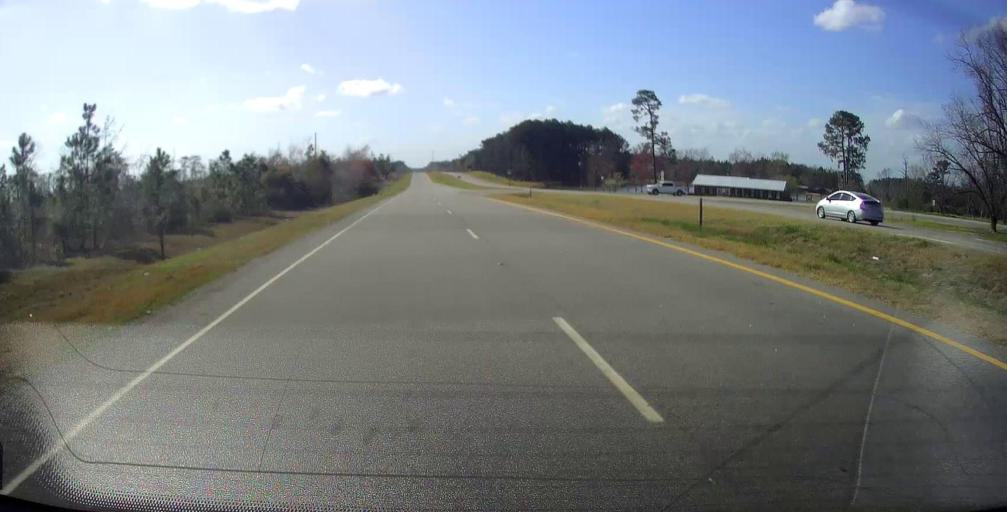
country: US
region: Georgia
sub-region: Dodge County
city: Eastman
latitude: 32.1991
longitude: -83.2335
